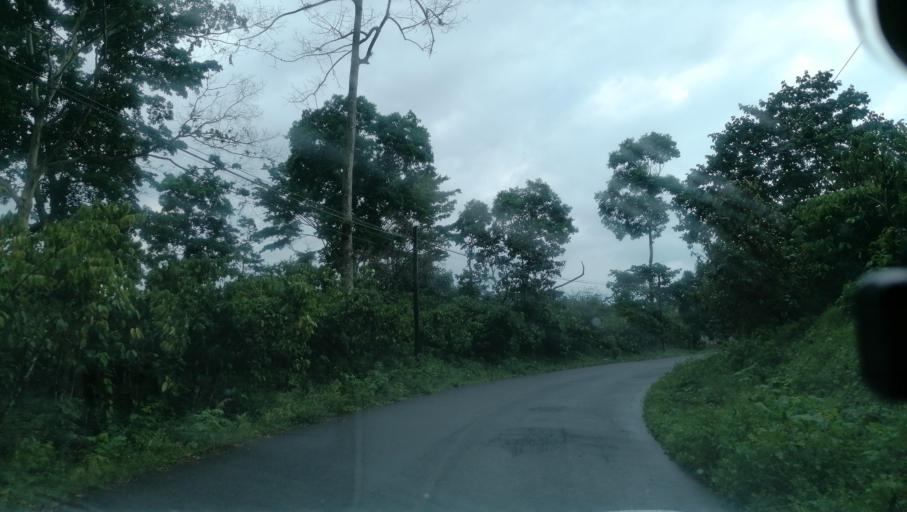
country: MX
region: Chiapas
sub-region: Cacahoatan
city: Benito Juarez
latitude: 15.0488
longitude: -92.1870
